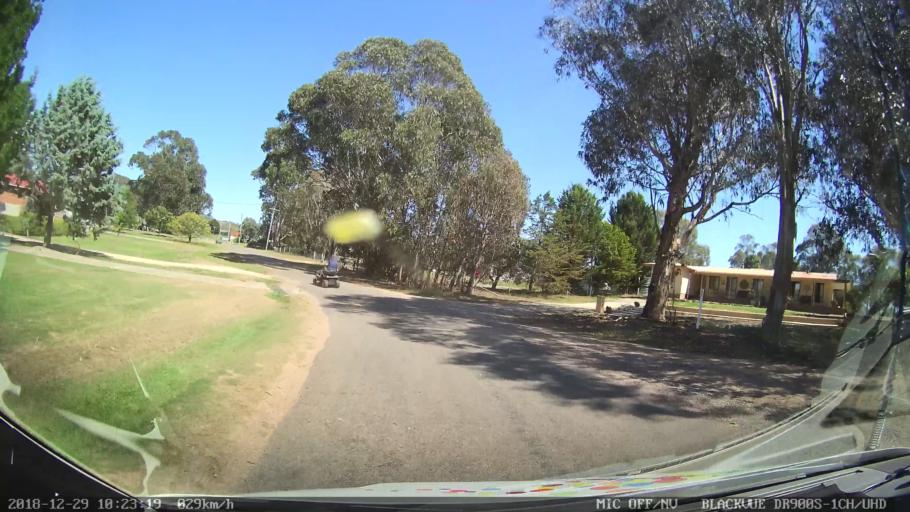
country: AU
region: New South Wales
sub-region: Yass Valley
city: Gundaroo
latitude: -34.9143
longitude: 149.4384
